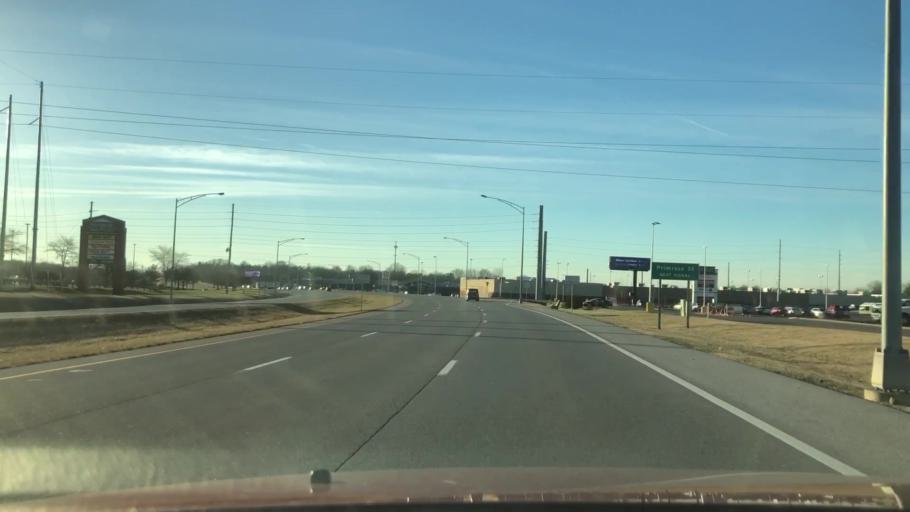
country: US
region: Missouri
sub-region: Greene County
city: Springfield
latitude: 37.1545
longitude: -93.2629
